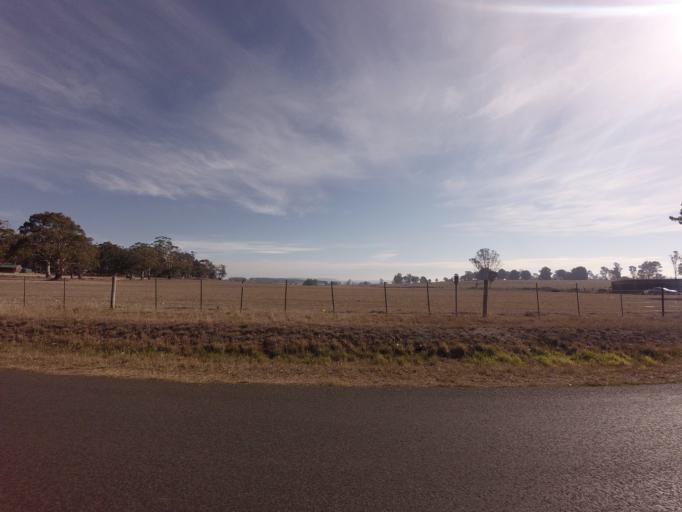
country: AU
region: Tasmania
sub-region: Sorell
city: Sorell
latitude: -42.4602
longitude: 147.4613
